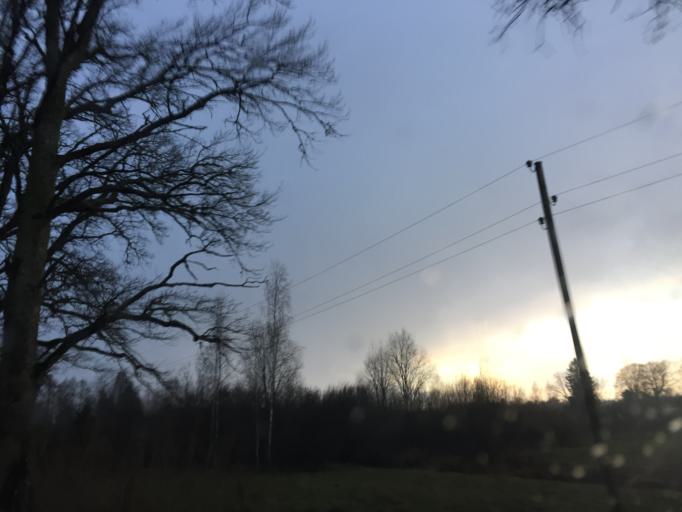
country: LV
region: Burtnieki
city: Matisi
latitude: 57.6893
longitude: 25.2553
